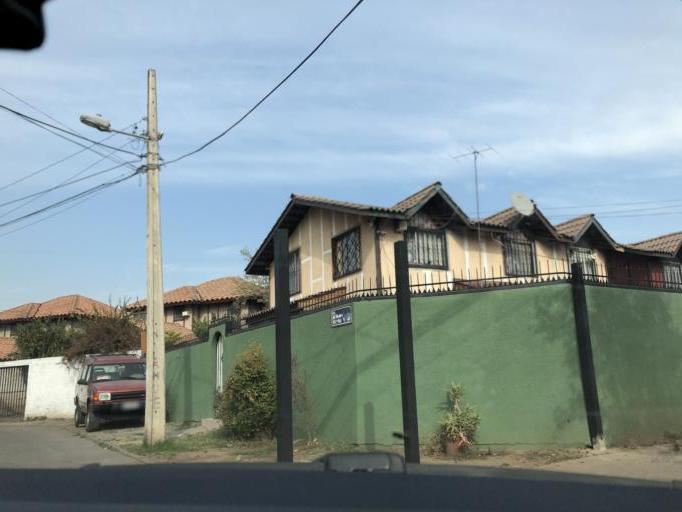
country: CL
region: Santiago Metropolitan
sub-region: Provincia de Cordillera
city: Puente Alto
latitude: -33.5479
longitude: -70.5619
